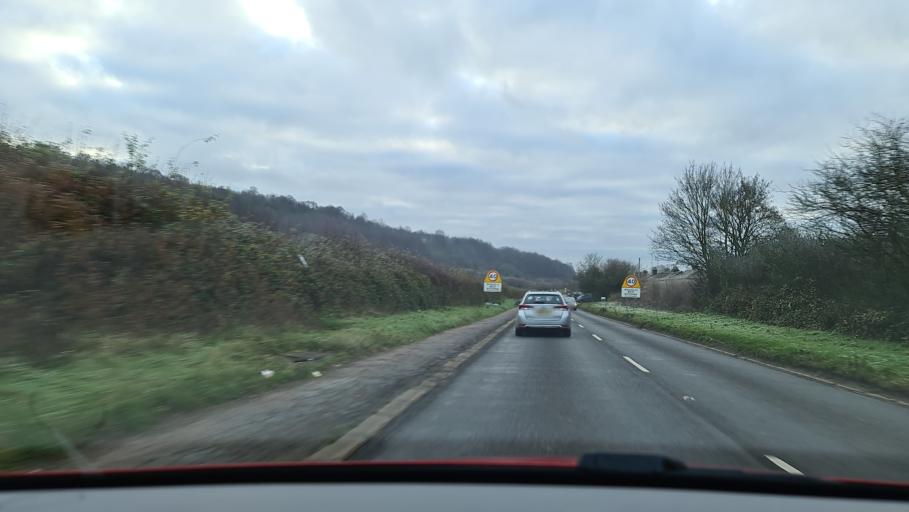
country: GB
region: England
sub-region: Buckinghamshire
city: High Wycombe
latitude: 51.6594
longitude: -0.8044
